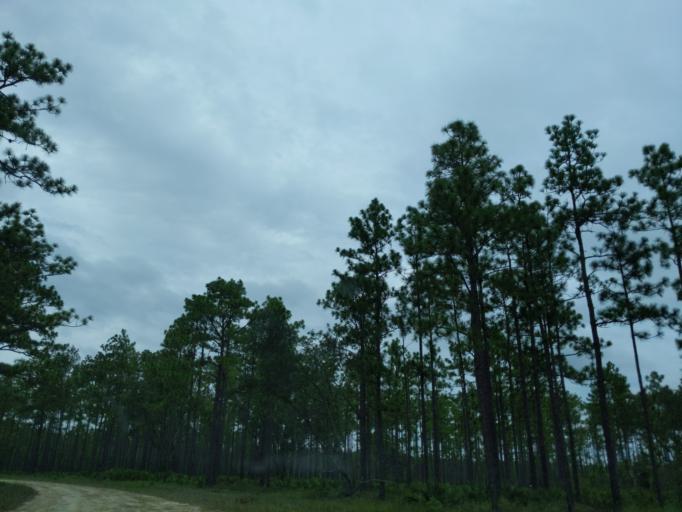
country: US
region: Florida
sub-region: Gadsden County
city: Midway
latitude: 30.3643
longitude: -84.4815
